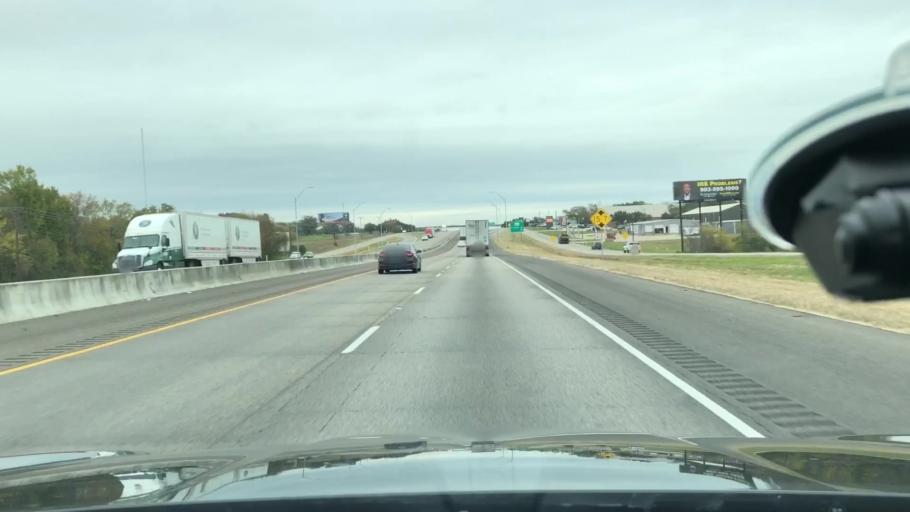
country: US
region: Texas
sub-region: Hopkins County
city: Sulphur Springs
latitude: 33.1311
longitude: -95.5770
